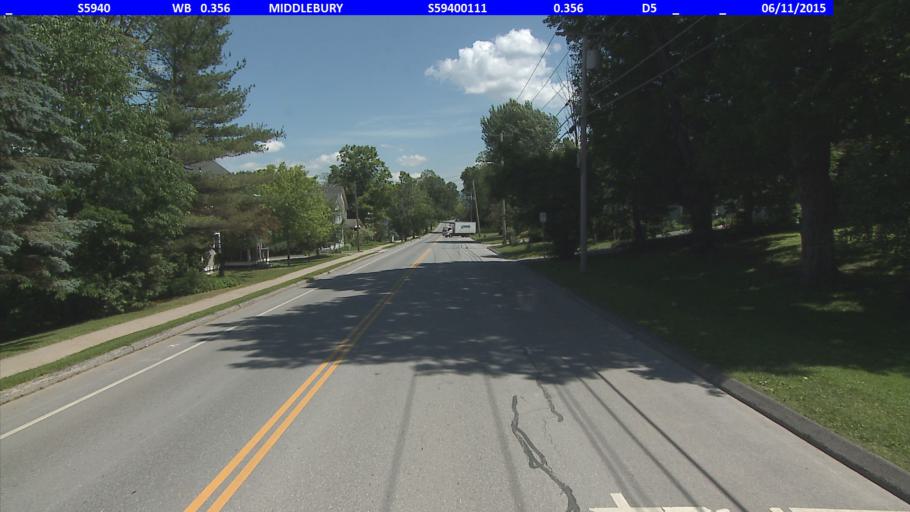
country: US
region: Vermont
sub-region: Addison County
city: Middlebury (village)
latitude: 44.0153
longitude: -73.1762
